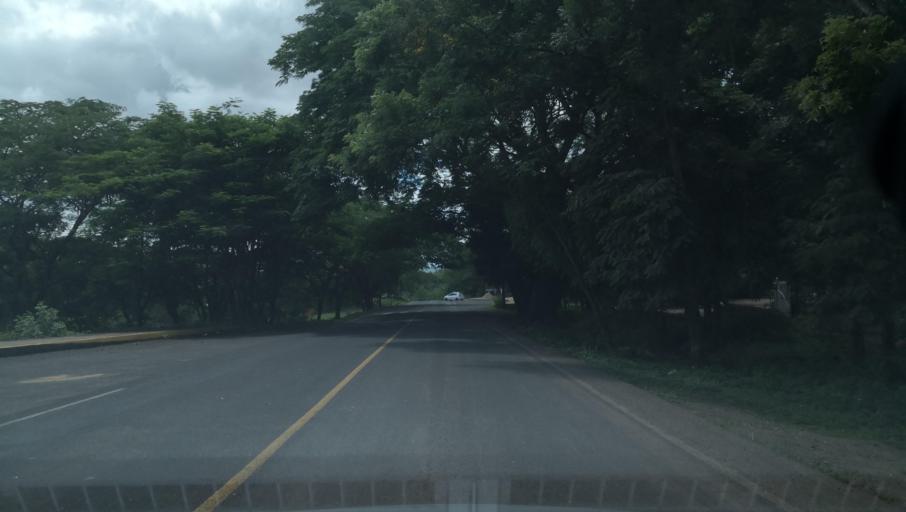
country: NI
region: Esteli
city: Condega
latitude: 13.4067
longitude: -86.4003
